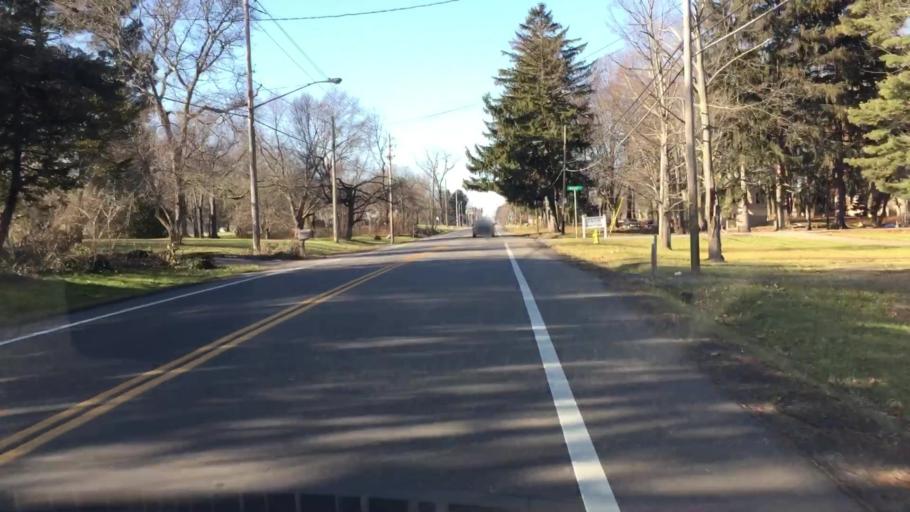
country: US
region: Ohio
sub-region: Summit County
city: Fairlawn
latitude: 41.0893
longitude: -81.6112
